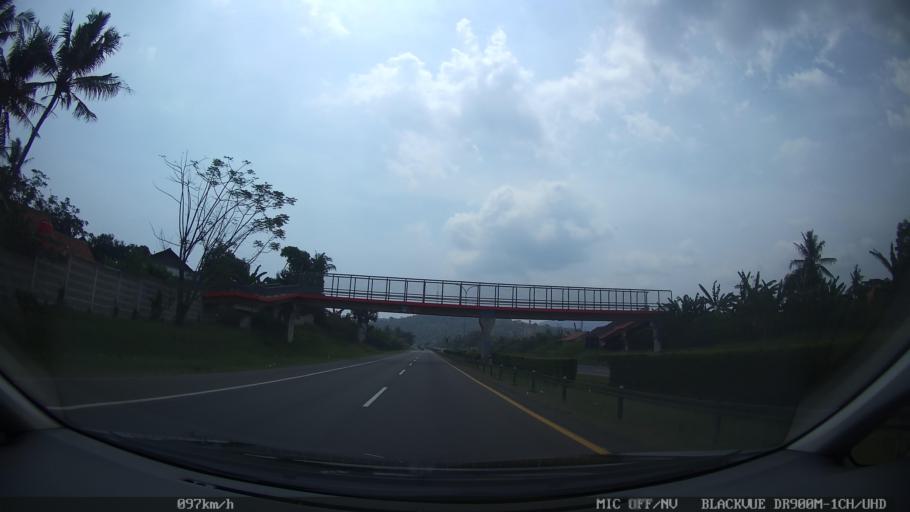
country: ID
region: Banten
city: Curug
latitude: -5.9932
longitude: 106.0531
